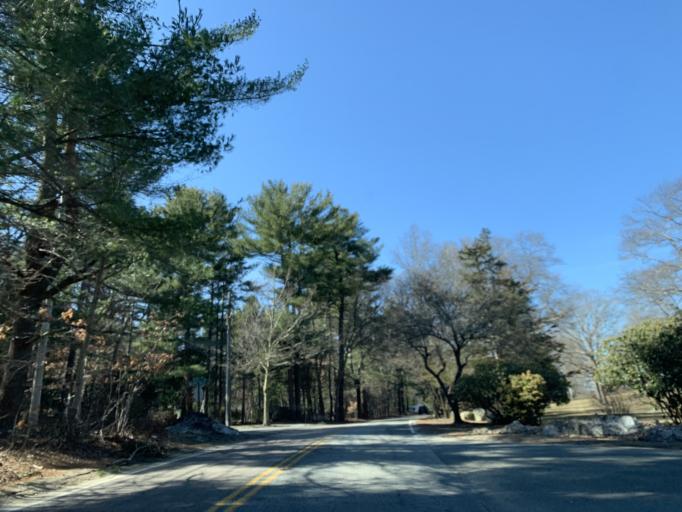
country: US
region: Massachusetts
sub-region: Norfolk County
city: Sharon
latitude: 42.1434
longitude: -71.1743
